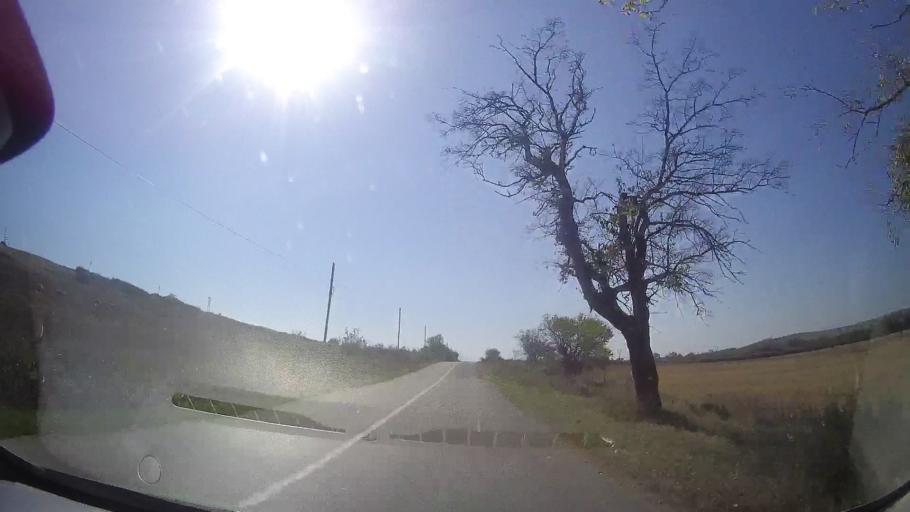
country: RO
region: Timis
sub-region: Comuna Bethausen
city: Bethausen
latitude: 45.8494
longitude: 21.9636
